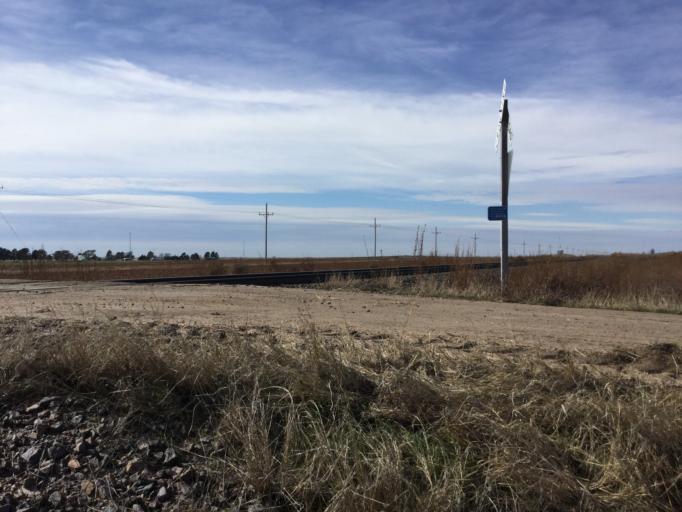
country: US
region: Kansas
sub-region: Trego County
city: WaKeeney
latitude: 39.0016
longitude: -99.7975
